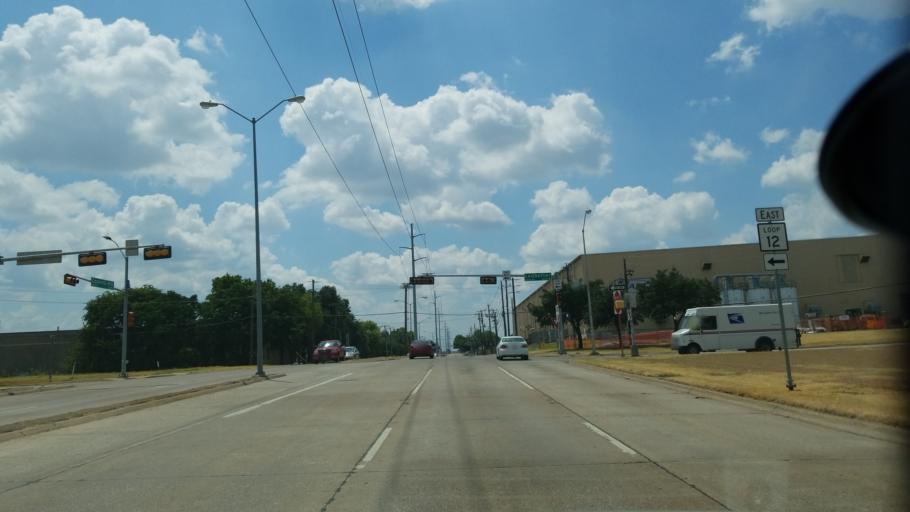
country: US
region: Texas
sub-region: Dallas County
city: Duncanville
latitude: 32.6913
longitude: -96.8915
